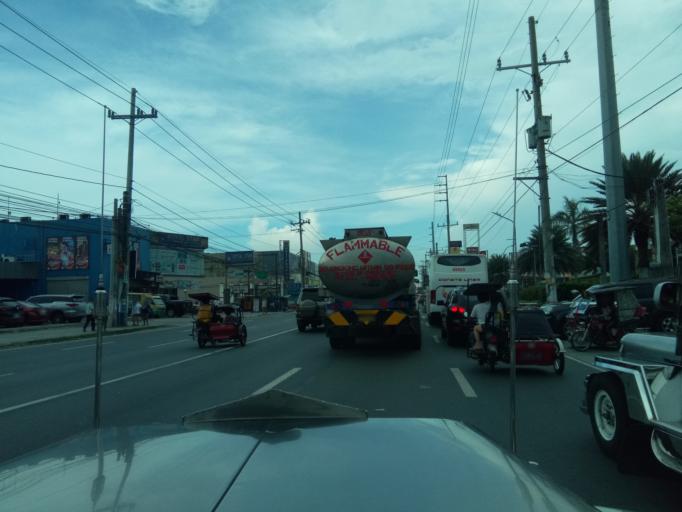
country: PH
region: Calabarzon
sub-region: Province of Cavite
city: Manggahan
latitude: 14.2918
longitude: 120.9084
